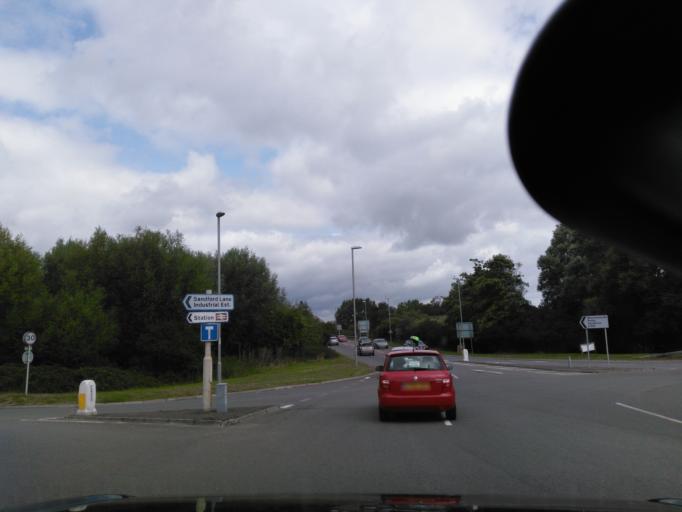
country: GB
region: England
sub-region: Dorset
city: Wareham
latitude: 50.6908
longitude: -2.1137
